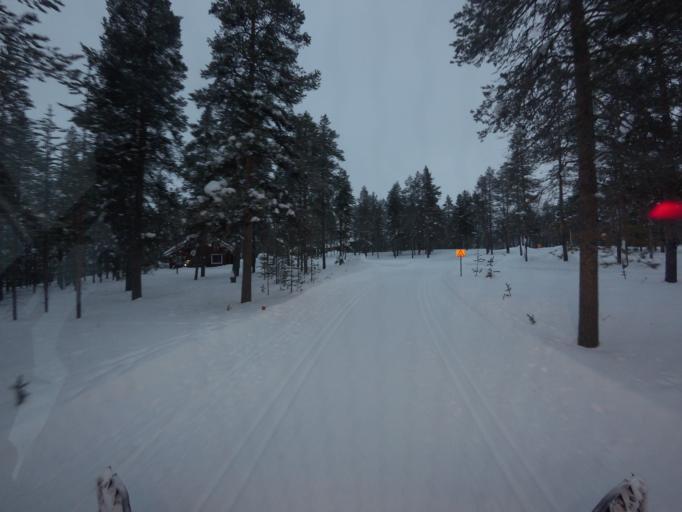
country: FI
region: Lapland
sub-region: Tunturi-Lappi
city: Kolari
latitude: 67.6200
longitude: 24.1692
